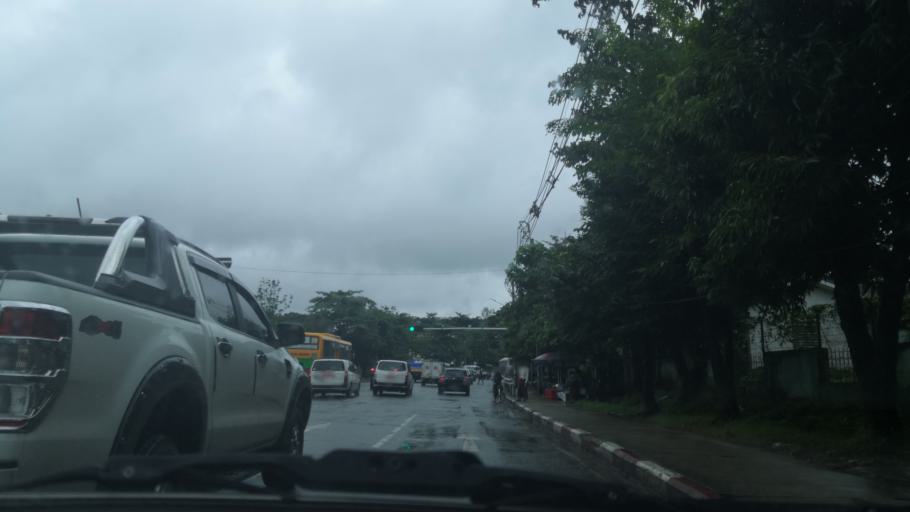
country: MM
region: Yangon
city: Yangon
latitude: 16.8926
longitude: 96.1200
